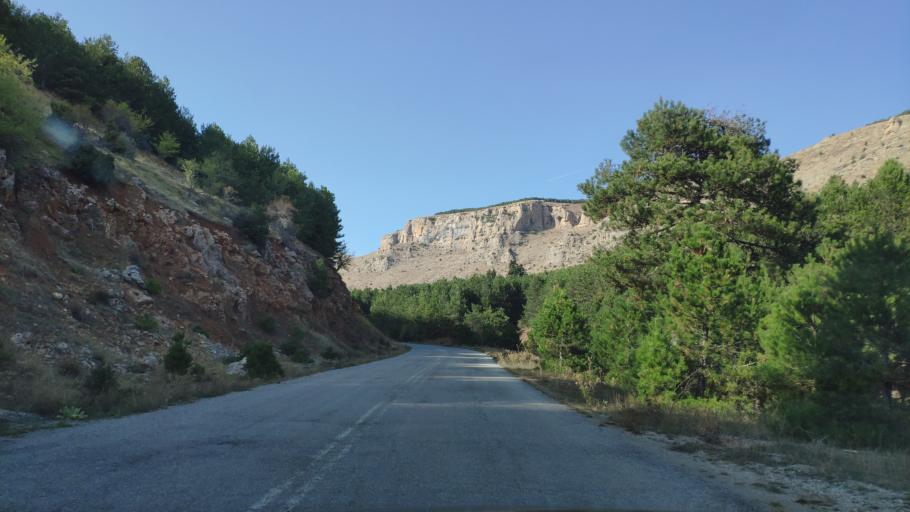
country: GR
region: West Greece
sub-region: Nomos Achaias
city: Aiyira
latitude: 38.0306
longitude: 22.4038
